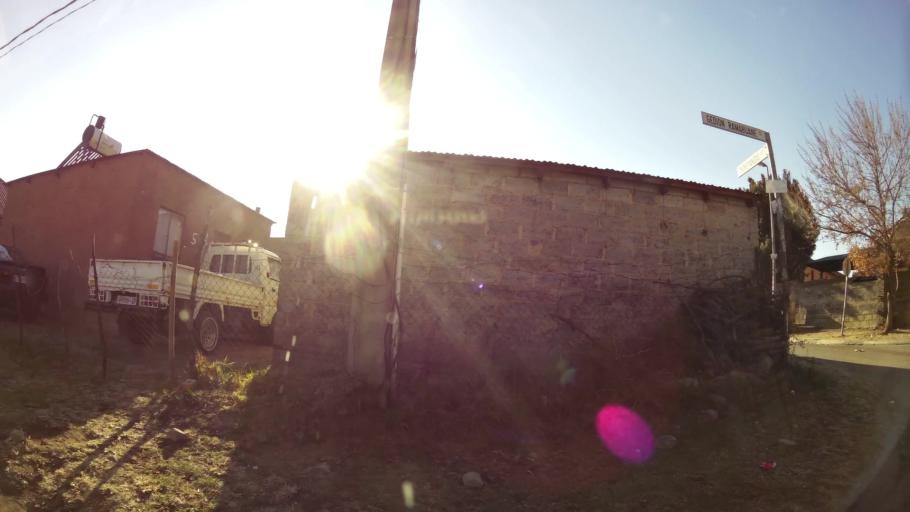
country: ZA
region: Gauteng
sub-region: City of Johannesburg Metropolitan Municipality
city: Modderfontein
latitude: -26.0459
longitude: 28.1589
